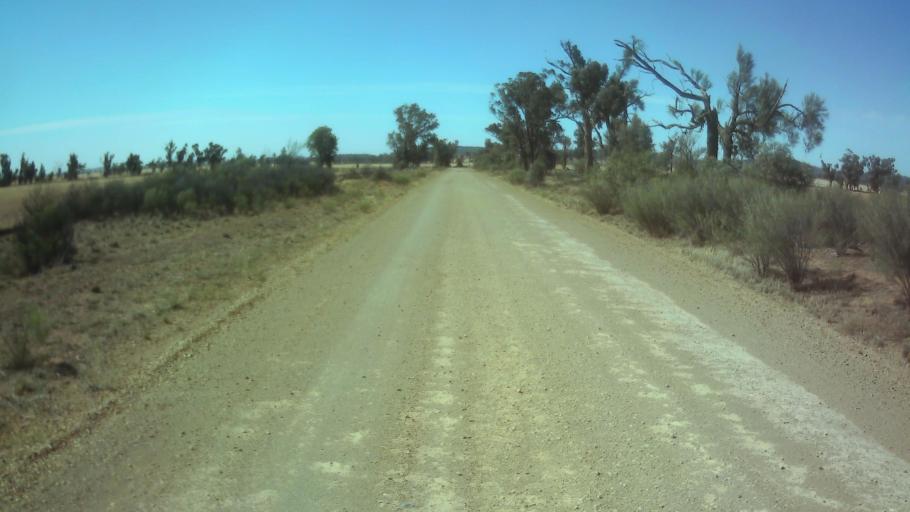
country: AU
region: New South Wales
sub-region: Forbes
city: Forbes
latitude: -33.7083
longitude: 147.7470
